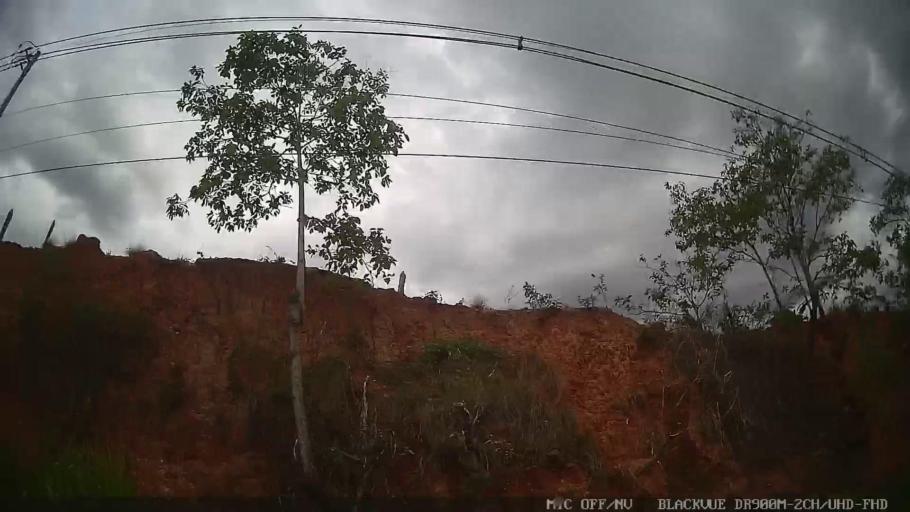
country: BR
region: Sao Paulo
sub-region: Amparo
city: Amparo
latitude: -22.7006
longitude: -46.7420
